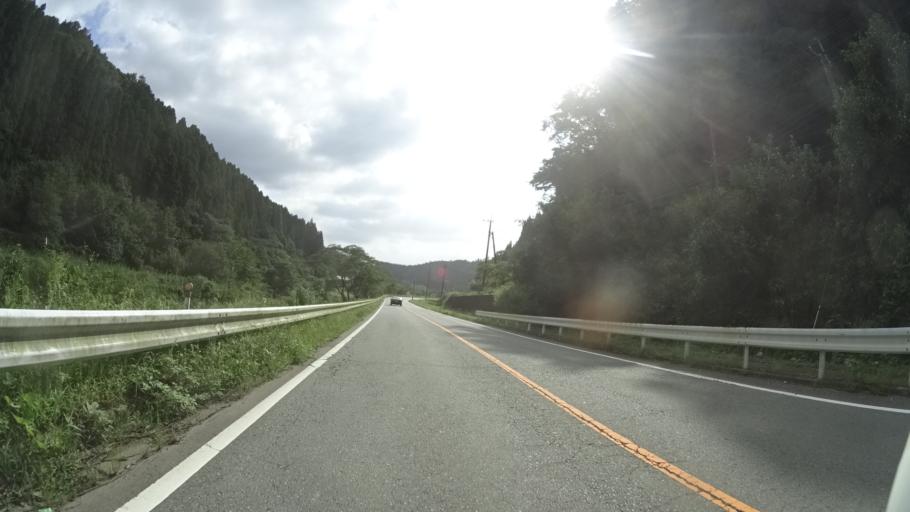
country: JP
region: Kumamoto
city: Aso
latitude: 32.6946
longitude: 131.1007
